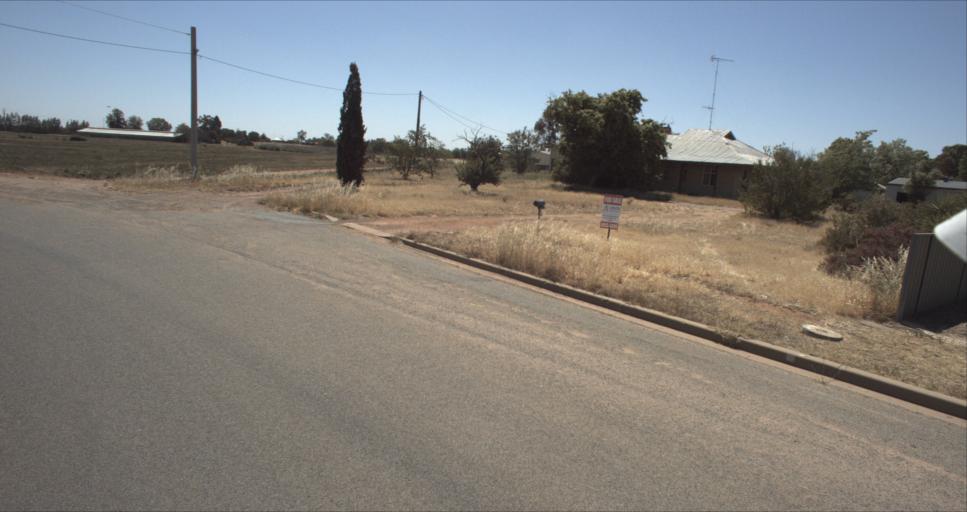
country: AU
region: New South Wales
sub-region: Leeton
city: Leeton
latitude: -34.5444
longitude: 146.3966
